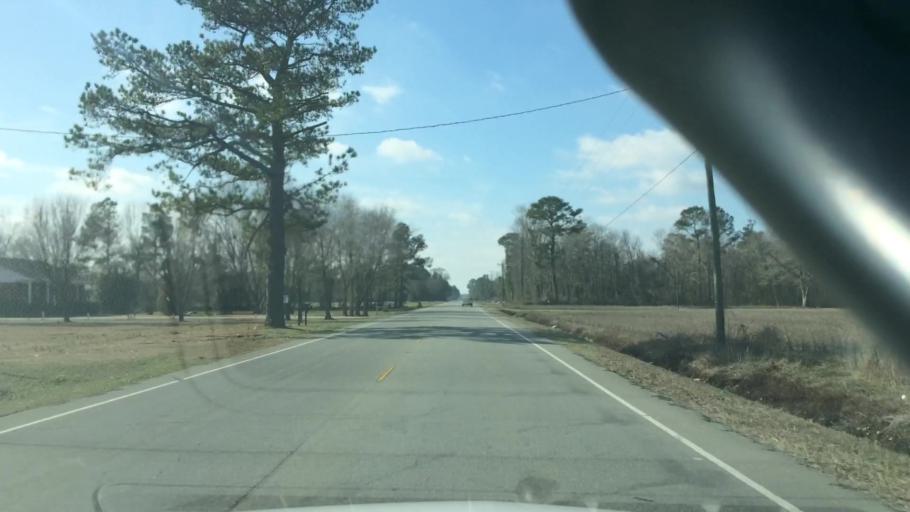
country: US
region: North Carolina
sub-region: Duplin County
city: Wallace
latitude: 34.7917
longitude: -77.8718
